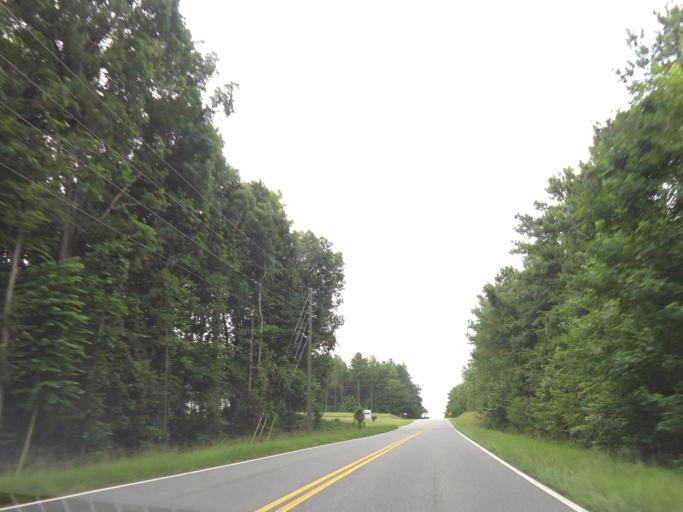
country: US
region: Georgia
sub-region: Bibb County
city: West Point
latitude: 32.8872
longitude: -83.7748
